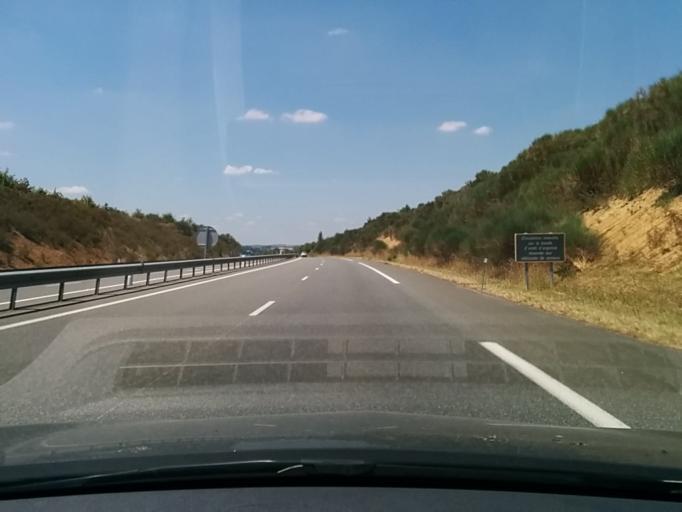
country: FR
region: Midi-Pyrenees
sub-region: Departement du Gers
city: Aubiet
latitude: 43.6403
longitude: 0.8173
